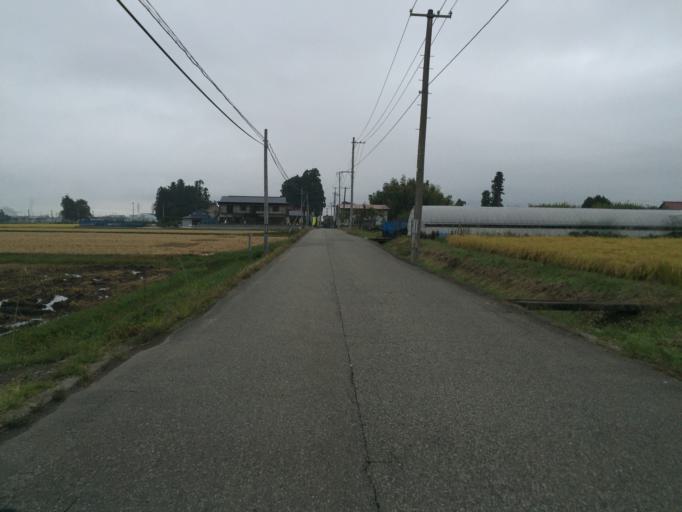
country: JP
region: Fukushima
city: Kitakata
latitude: 37.4470
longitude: 139.9149
